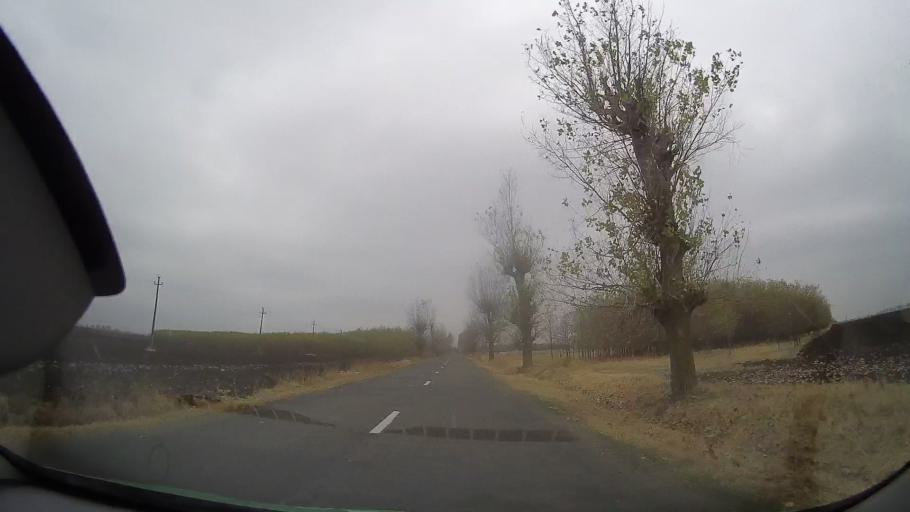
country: RO
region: Ialomita
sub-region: Comuna Grindu
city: Grindu
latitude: 44.7859
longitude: 26.9032
